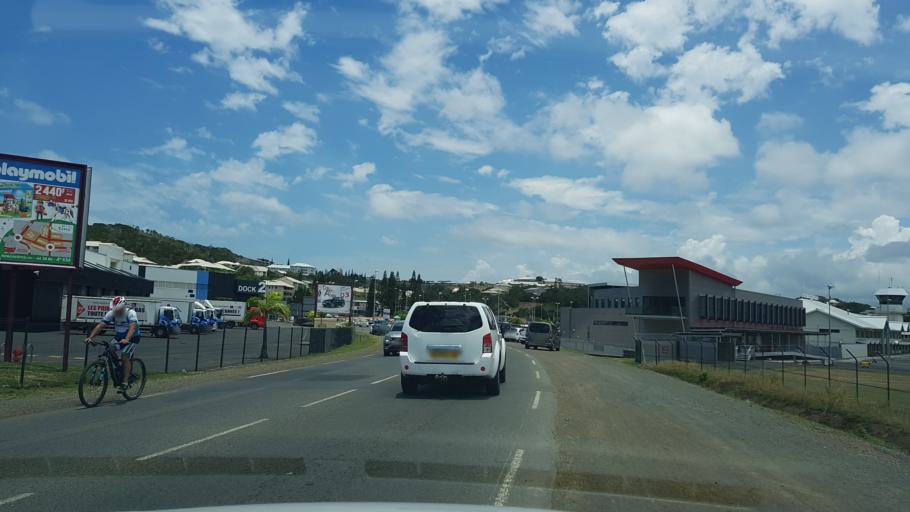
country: NC
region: South Province
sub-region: Noumea
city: Noumea
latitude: -22.2623
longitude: 166.4719
